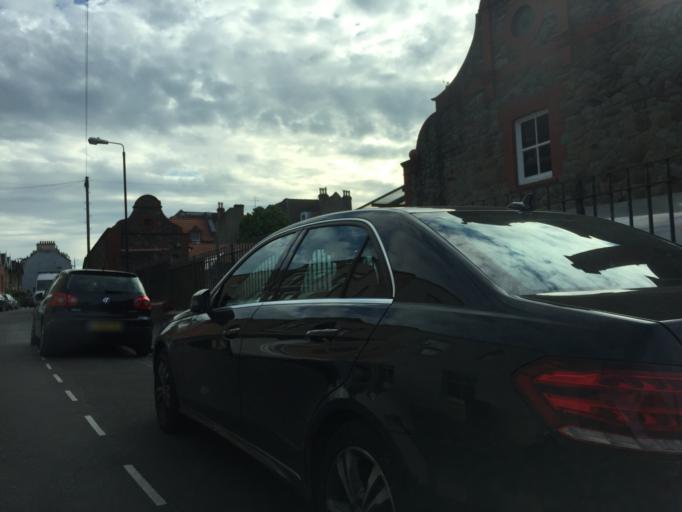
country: GB
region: England
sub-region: Bristol
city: Bristol
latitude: 51.4693
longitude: -2.5819
